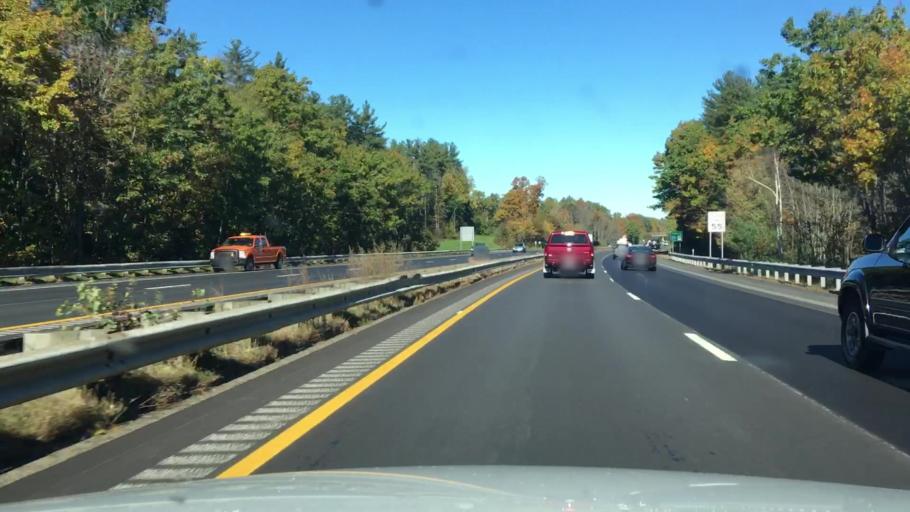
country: US
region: New Hampshire
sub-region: Strafford County
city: Dover
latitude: 43.1934
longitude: -70.8939
